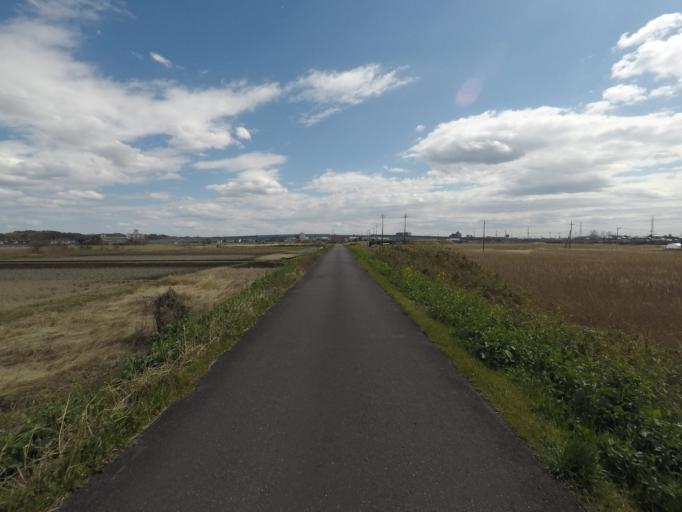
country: JP
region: Ibaraki
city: Fujishiro
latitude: 35.9388
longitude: 140.1278
